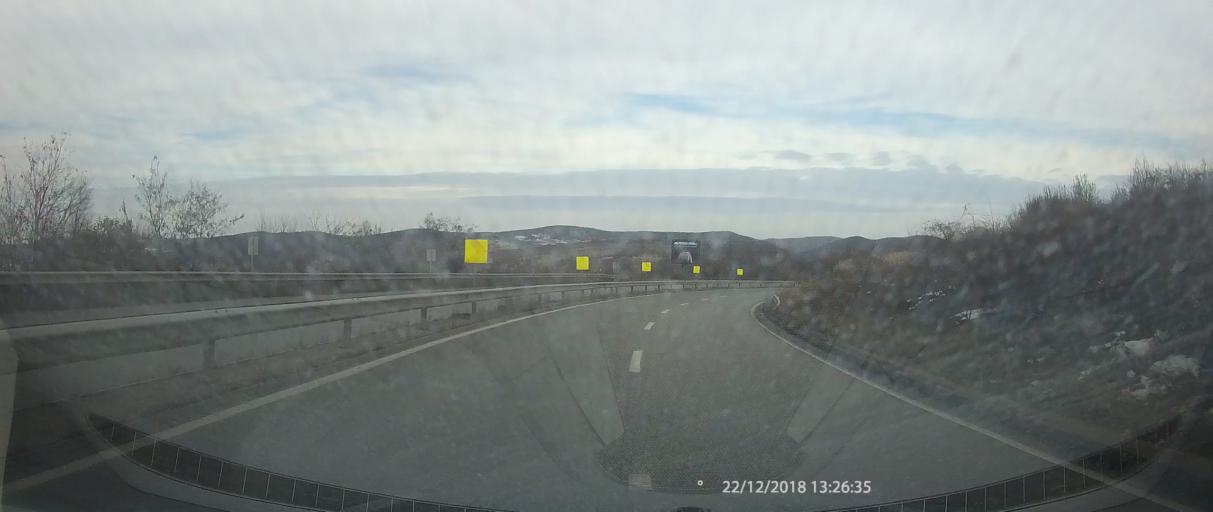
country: BG
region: Lovech
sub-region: Obshtina Yablanitsa
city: Yablanitsa
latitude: 43.0462
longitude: 24.1223
